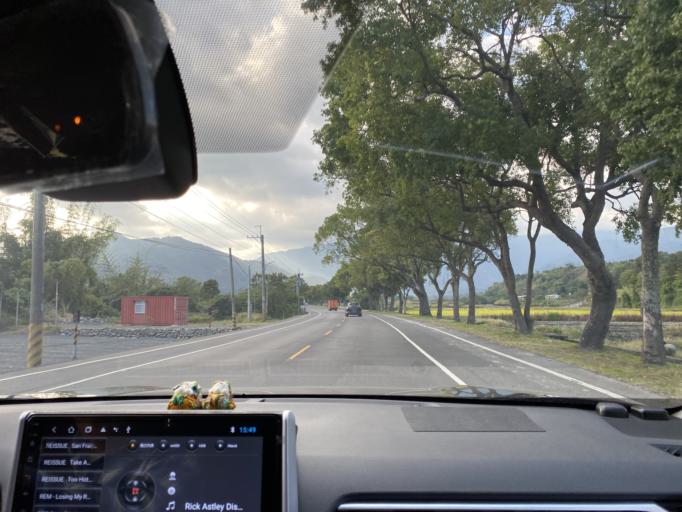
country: TW
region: Taiwan
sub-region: Taitung
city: Taitung
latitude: 22.8939
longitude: 121.1292
